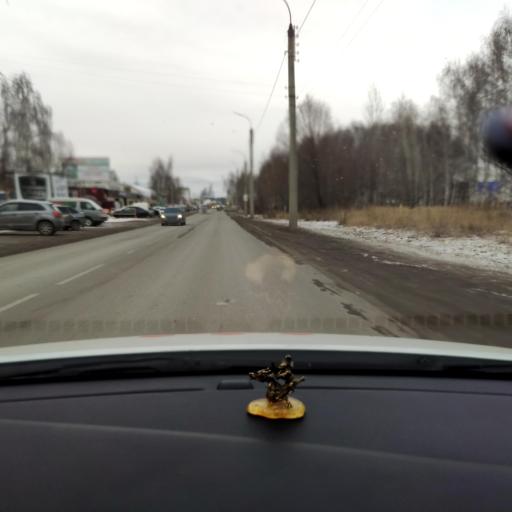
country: RU
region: Tatarstan
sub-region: Zelenodol'skiy Rayon
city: Zelenodolsk
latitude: 55.8645
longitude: 48.5481
